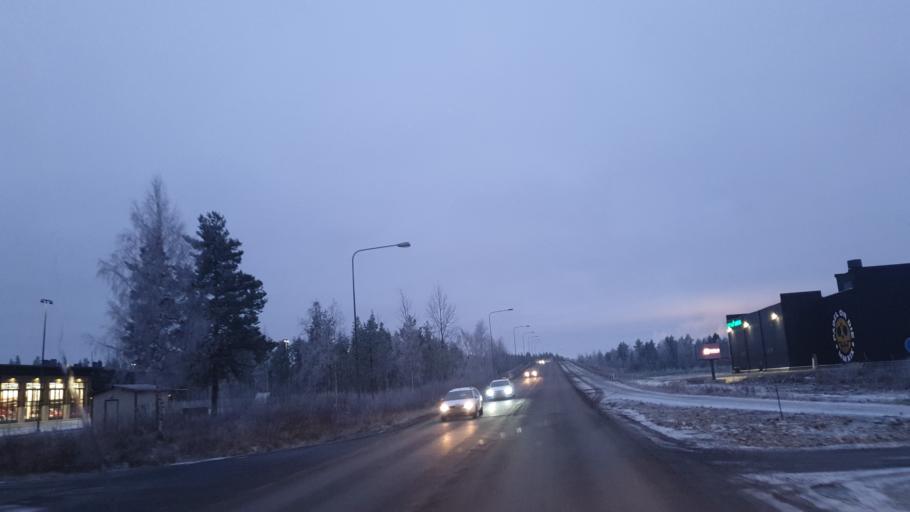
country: FI
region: Southern Ostrobothnia
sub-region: Seinaejoki
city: Nurmo
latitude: 62.7767
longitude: 22.8925
